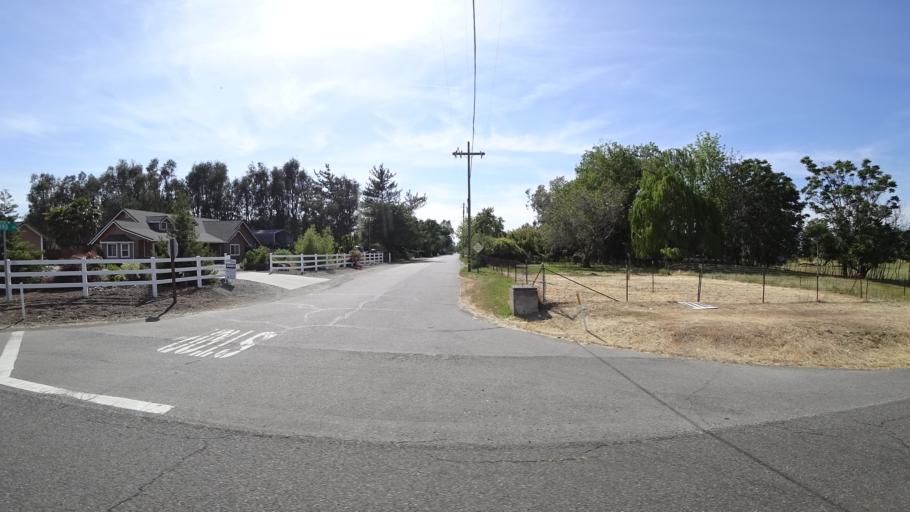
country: US
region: California
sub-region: Tehama County
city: Los Molinos
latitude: 40.0636
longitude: -122.1007
